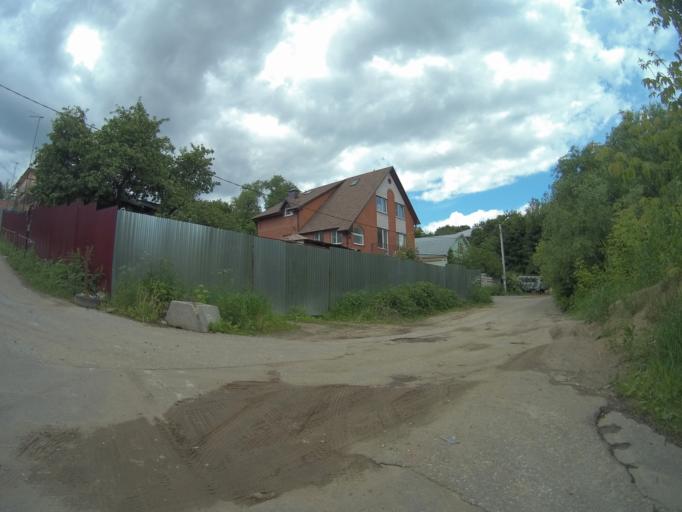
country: RU
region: Vladimir
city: Vladimir
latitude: 56.1218
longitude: 40.3897
